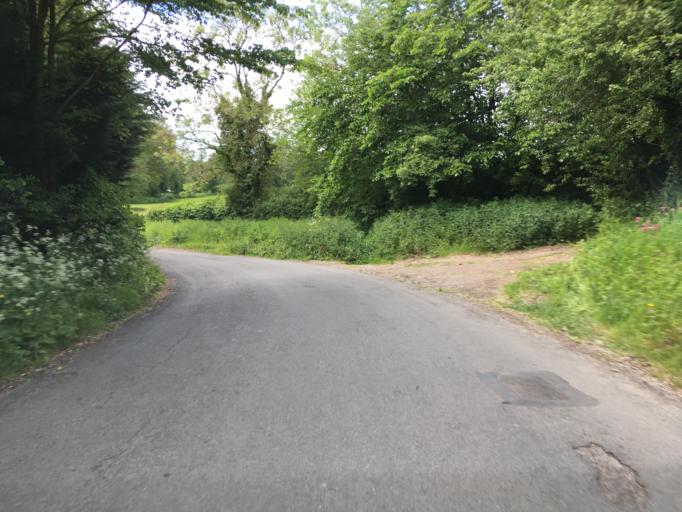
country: GB
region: England
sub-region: Gloucestershire
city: Dursley
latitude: 51.6696
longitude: -2.3839
